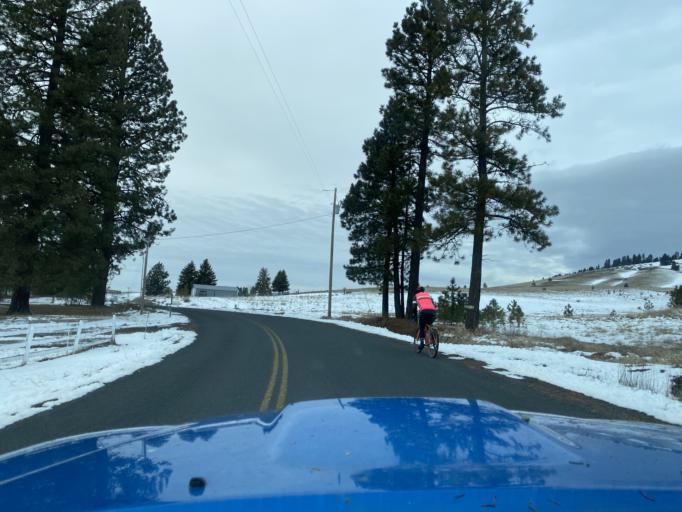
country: US
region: Idaho
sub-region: Latah County
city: Moscow
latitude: 46.6940
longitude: -116.9182
